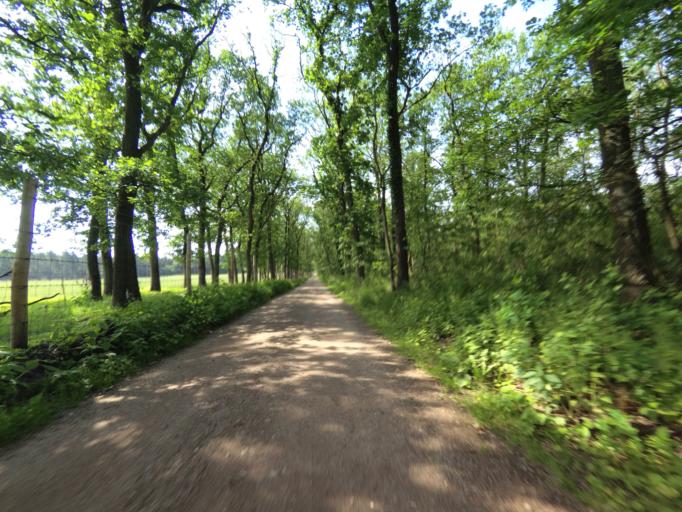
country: NL
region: Gelderland
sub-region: Gemeente Apeldoorn
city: Beekbergen
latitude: 52.1144
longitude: 5.8829
